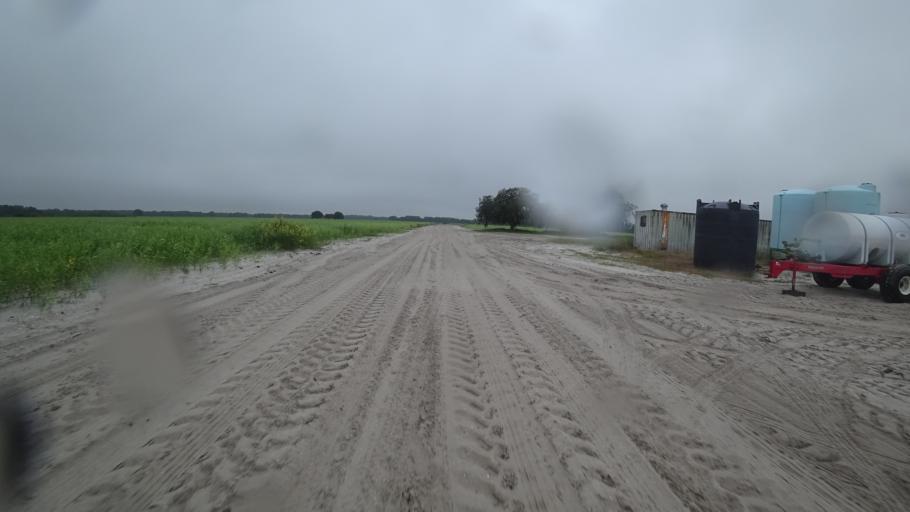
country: US
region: Florida
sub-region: Sarasota County
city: Warm Mineral Springs
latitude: 27.2935
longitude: -82.1607
